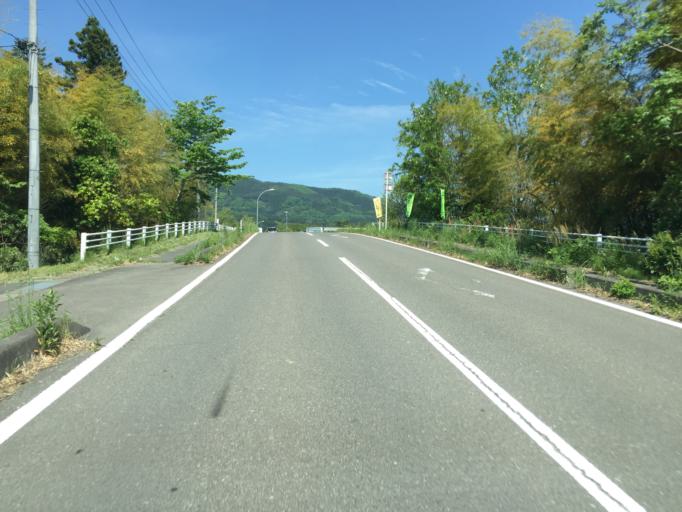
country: JP
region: Fukushima
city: Fukushima-shi
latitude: 37.7259
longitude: 140.3735
